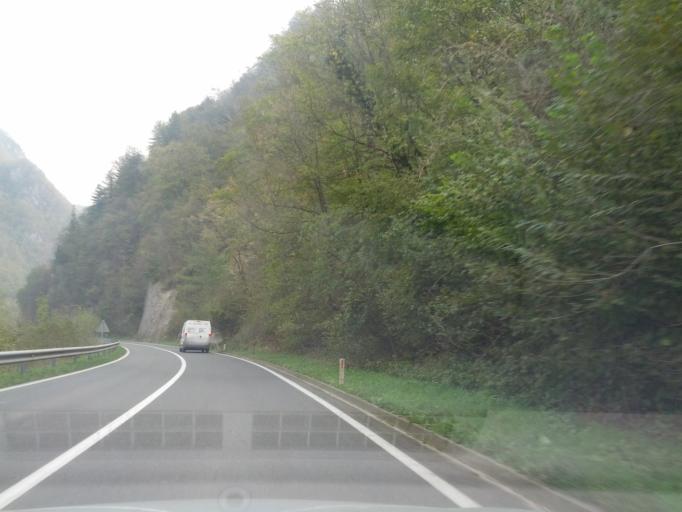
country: SI
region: Trbovlje
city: Trbovlje
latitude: 46.1246
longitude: 15.0591
